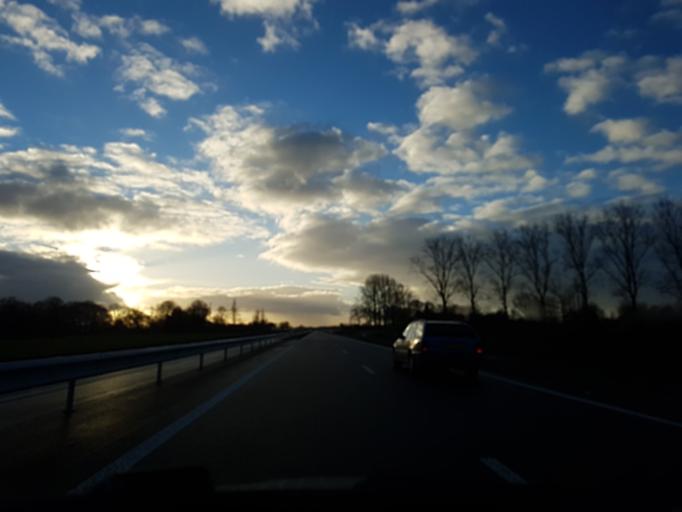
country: NL
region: Friesland
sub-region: Gemeente Tytsjerksteradiel
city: Hurdegaryp
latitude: 53.2222
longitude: 5.9421
